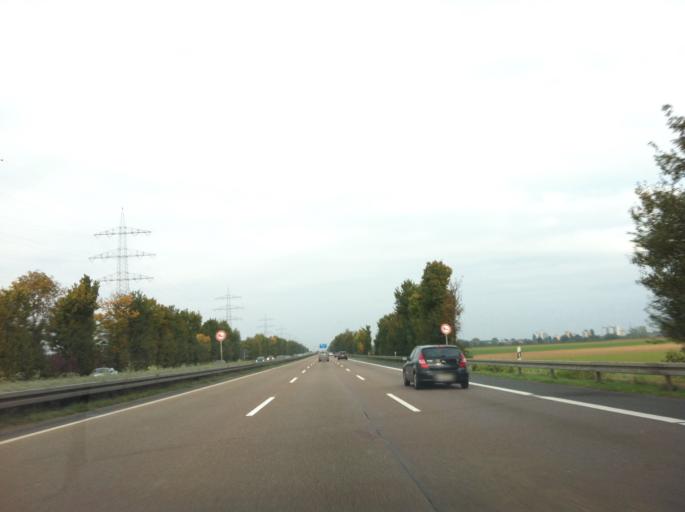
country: DE
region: Hesse
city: Liederbach
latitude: 50.1015
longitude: 8.4959
